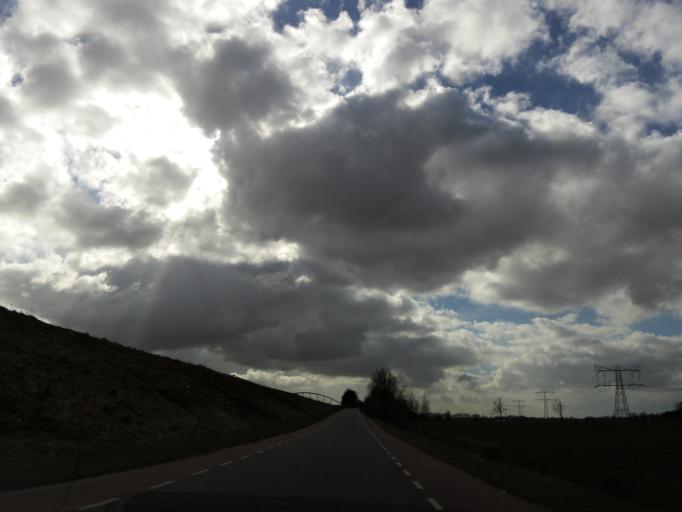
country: NL
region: Limburg
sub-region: Gemeente Sittard-Geleen
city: Born
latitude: 51.0616
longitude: 5.8099
